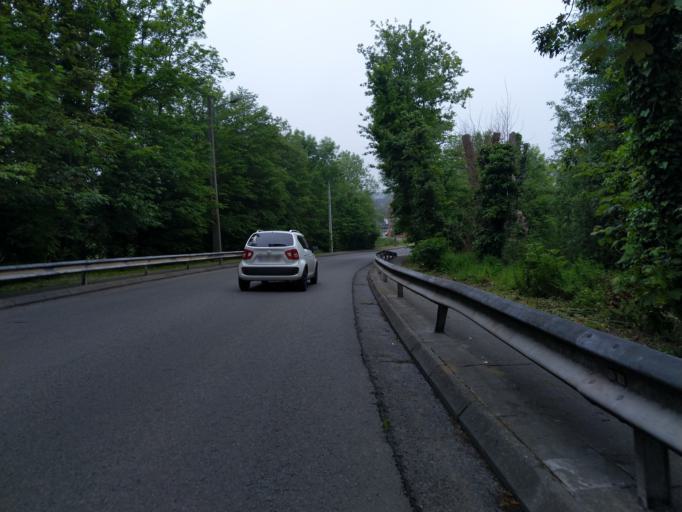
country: BE
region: Wallonia
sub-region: Province du Hainaut
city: Quaregnon
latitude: 50.4522
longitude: 3.8908
